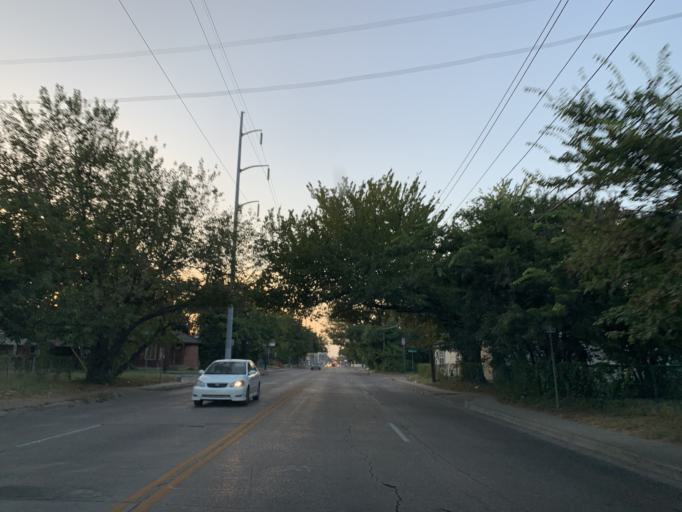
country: US
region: Texas
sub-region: Dallas County
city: Dallas
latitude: 32.7646
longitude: -96.7630
